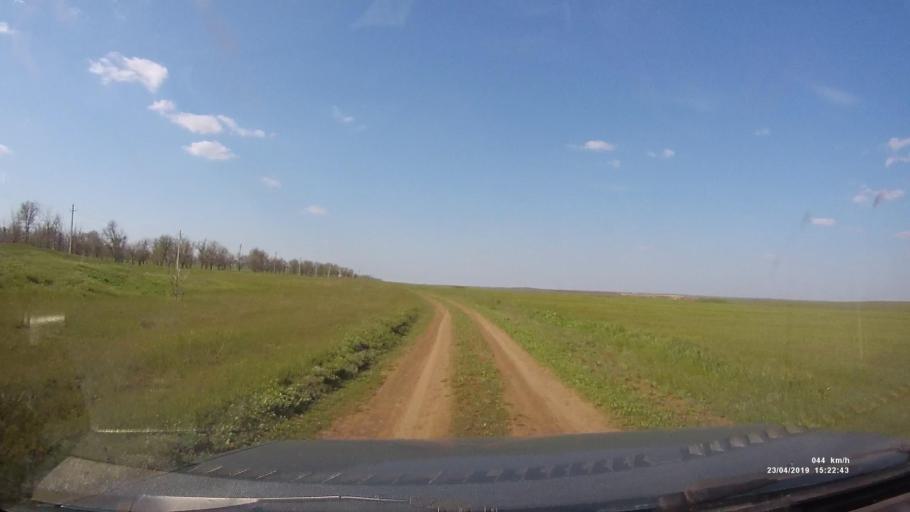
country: RU
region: Rostov
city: Remontnoye
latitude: 46.5308
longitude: 42.9704
